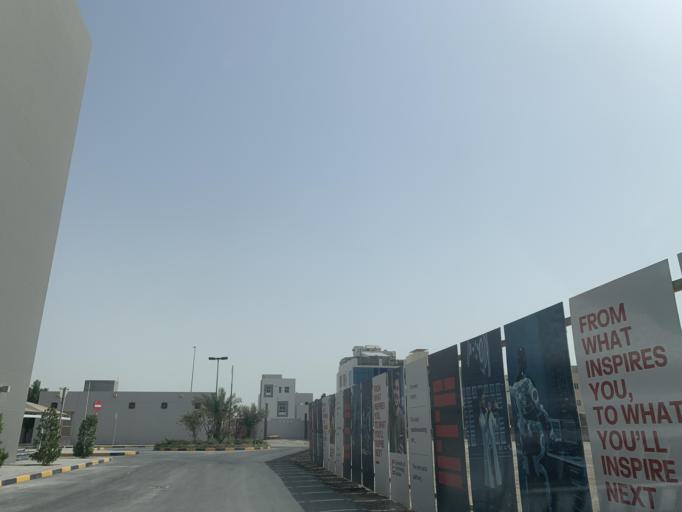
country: BH
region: Northern
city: Madinat `Isa
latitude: 26.1840
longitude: 50.5185
